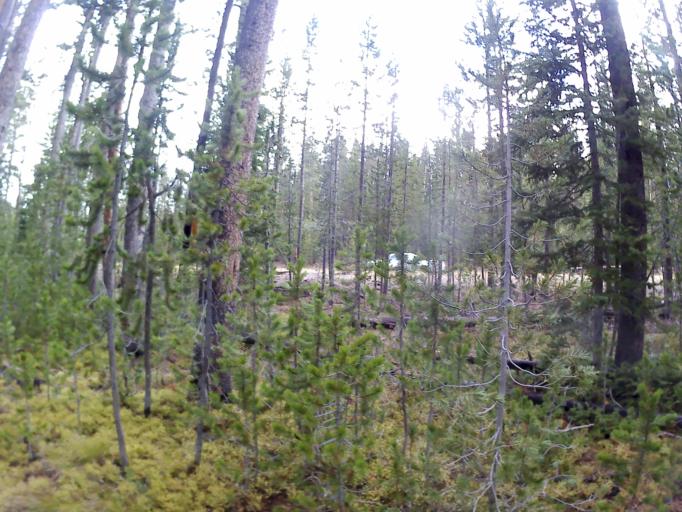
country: US
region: Montana
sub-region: Gallatin County
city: West Yellowstone
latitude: 44.4302
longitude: -110.7498
